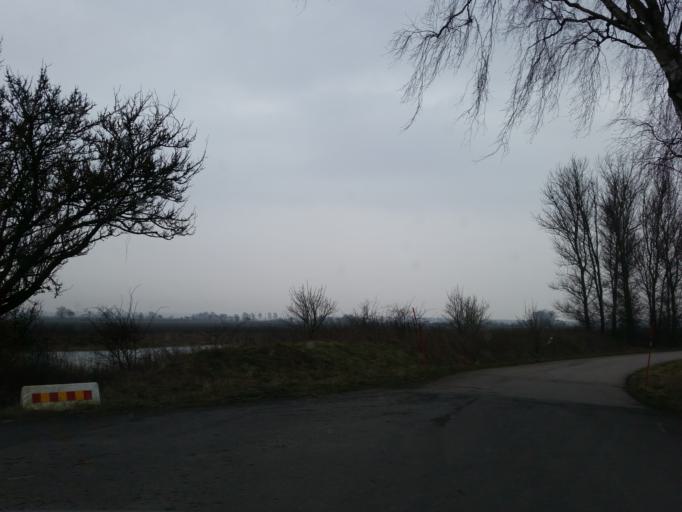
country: SE
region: Kalmar
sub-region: Morbylanga Kommun
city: Moerbylanga
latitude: 56.4629
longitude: 16.3981
